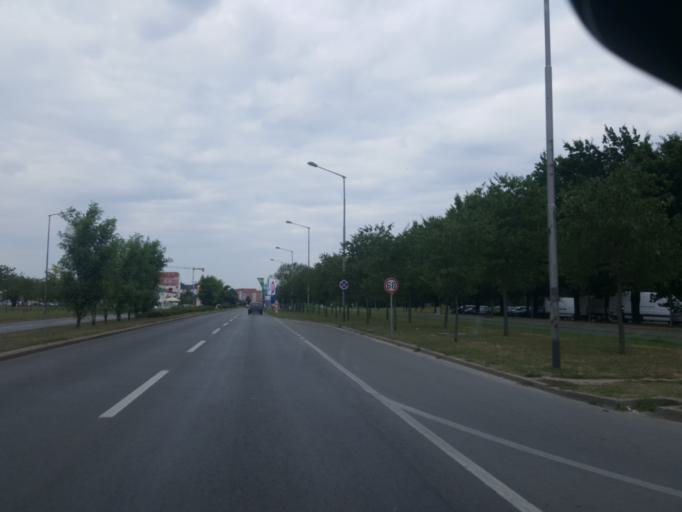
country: RS
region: Autonomna Pokrajina Vojvodina
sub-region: Juznobacki Okrug
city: Novi Sad
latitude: 45.2584
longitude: 19.8036
